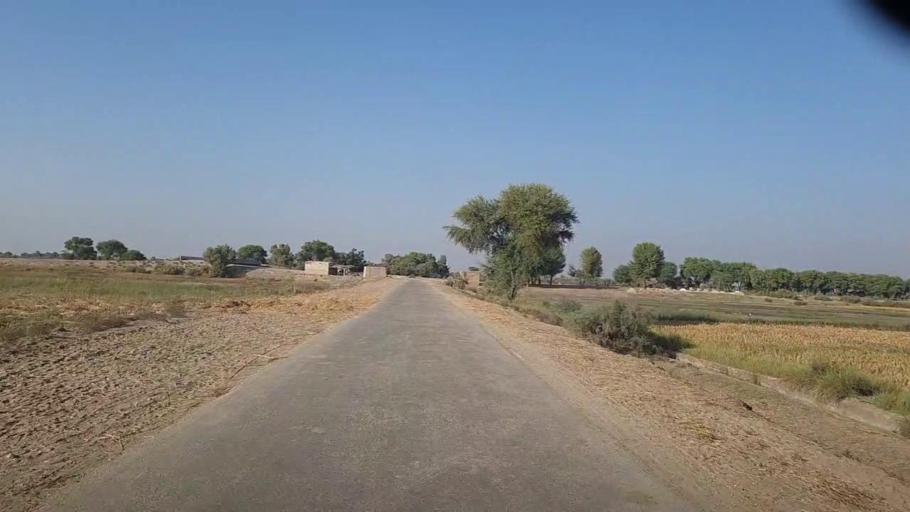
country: PK
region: Sindh
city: Tangwani
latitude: 28.2990
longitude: 68.9519
